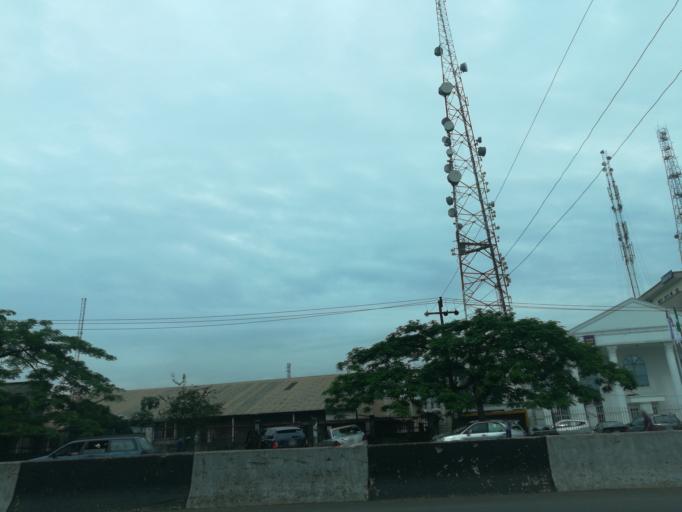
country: NG
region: Rivers
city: Port Harcourt
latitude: 4.8040
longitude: 7.0082
